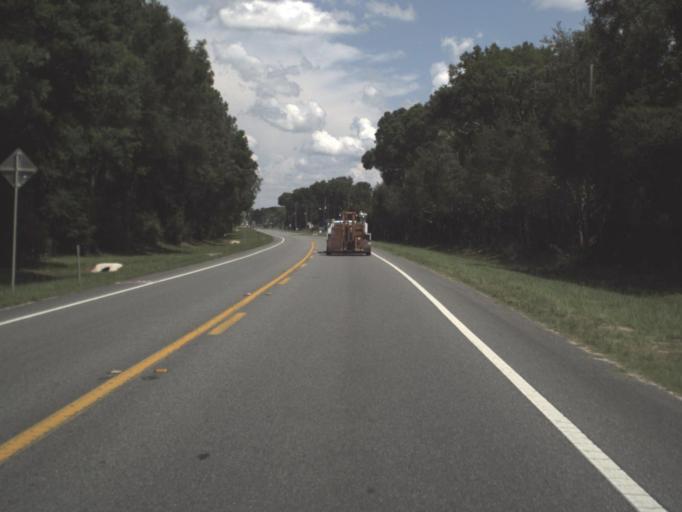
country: US
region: Florida
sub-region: Alachua County
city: High Springs
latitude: 29.8403
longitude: -82.6268
